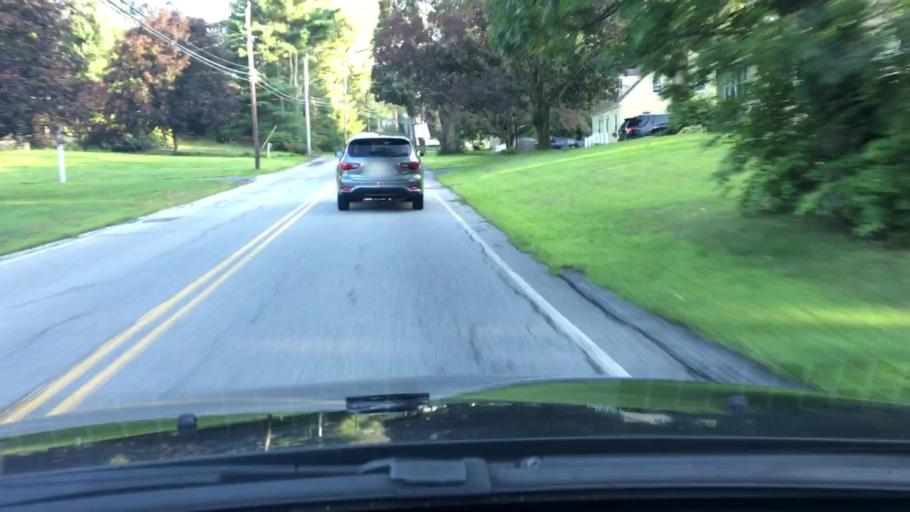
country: US
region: Massachusetts
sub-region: Worcester County
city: West Boylston
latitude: 42.3566
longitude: -71.7787
